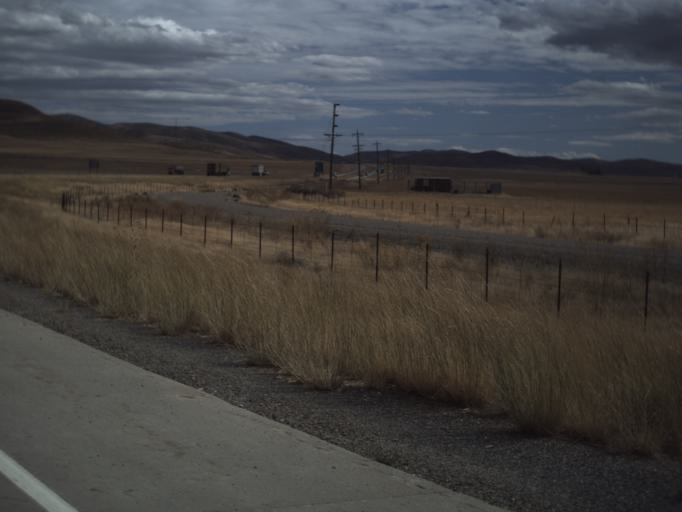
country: US
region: Utah
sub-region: Box Elder County
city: Garland
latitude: 41.8391
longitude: -112.4368
